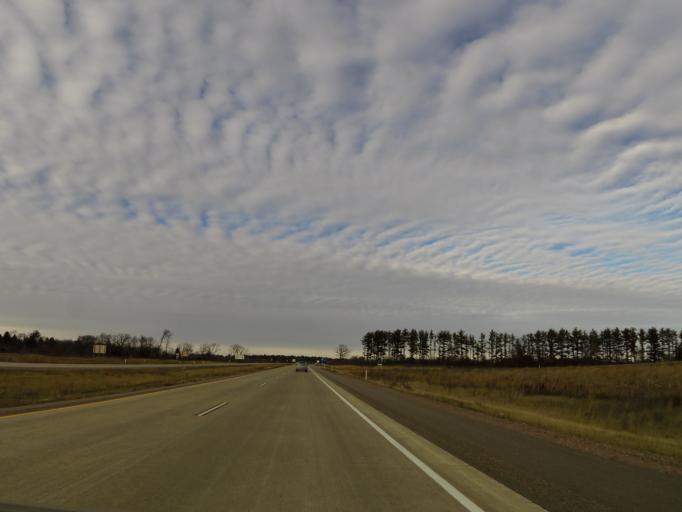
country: US
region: Wisconsin
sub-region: Sauk County
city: West Baraboo
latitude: 43.5157
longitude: -89.7844
